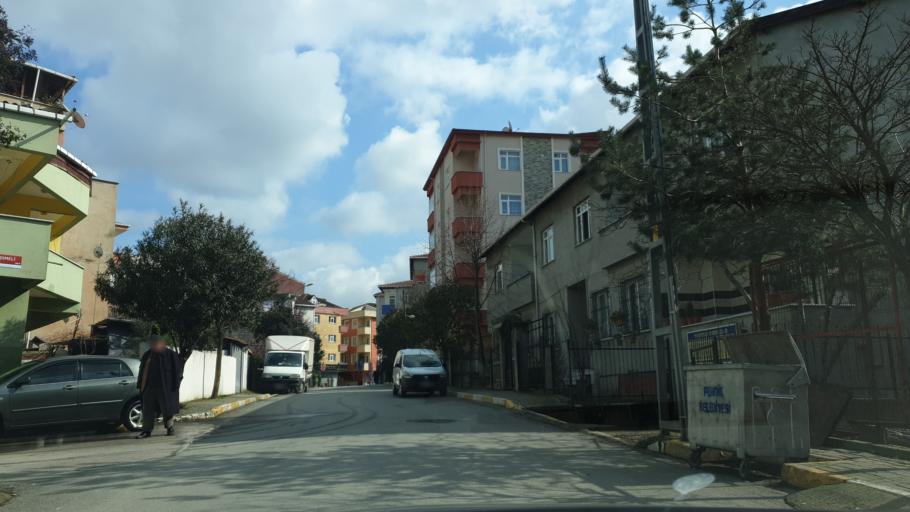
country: TR
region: Istanbul
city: Icmeler
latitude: 40.8672
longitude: 29.3047
